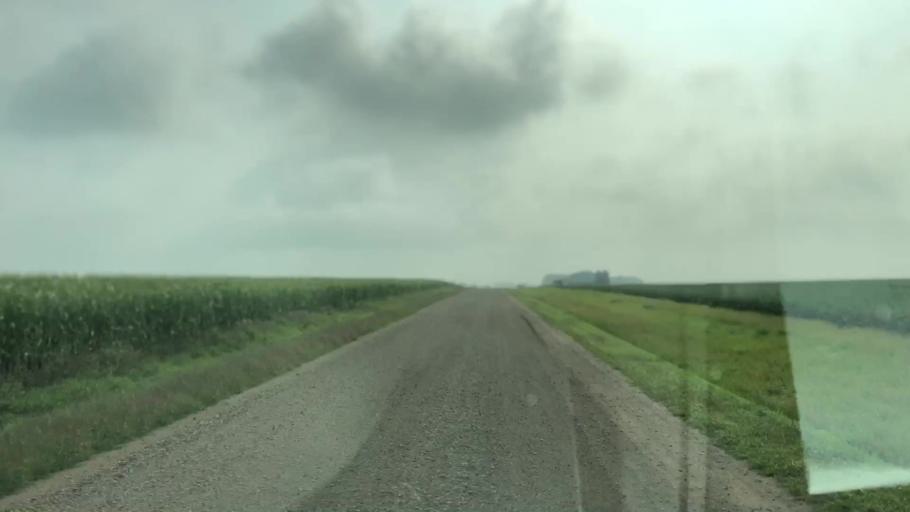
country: US
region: Iowa
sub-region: Sioux County
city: Hull
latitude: 43.2298
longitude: -96.0561
